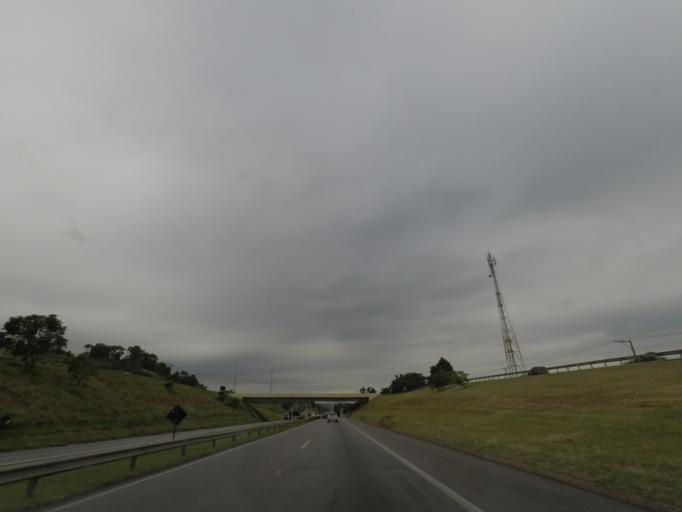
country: BR
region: Sao Paulo
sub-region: Jarinu
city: Jarinu
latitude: -23.0688
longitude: -46.6426
